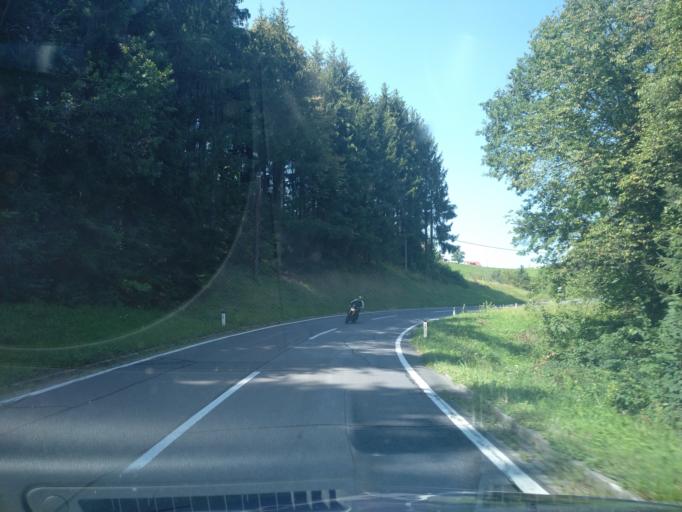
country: AT
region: Styria
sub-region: Politischer Bezirk Leibnitz
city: Leutschach
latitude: 46.6747
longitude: 15.4791
